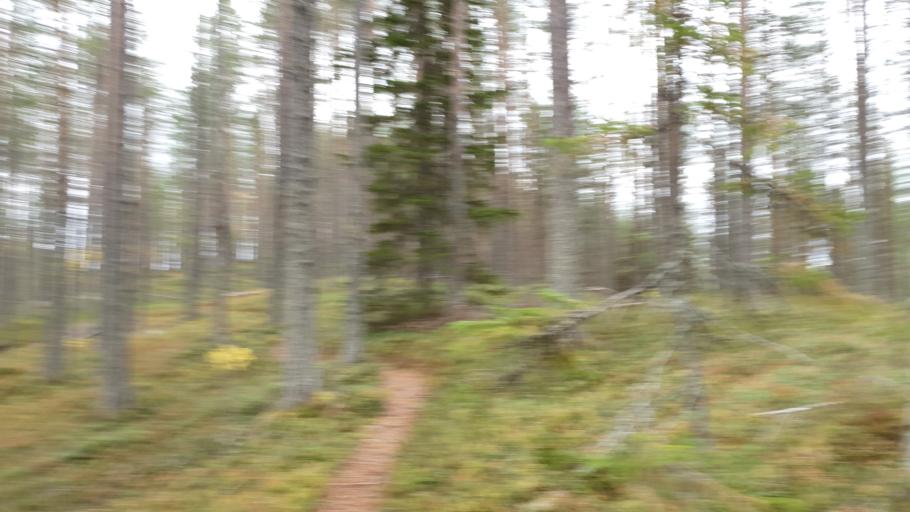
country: FI
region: Kainuu
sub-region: Kehys-Kainuu
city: Kuhmo
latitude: 64.2928
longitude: 29.3311
